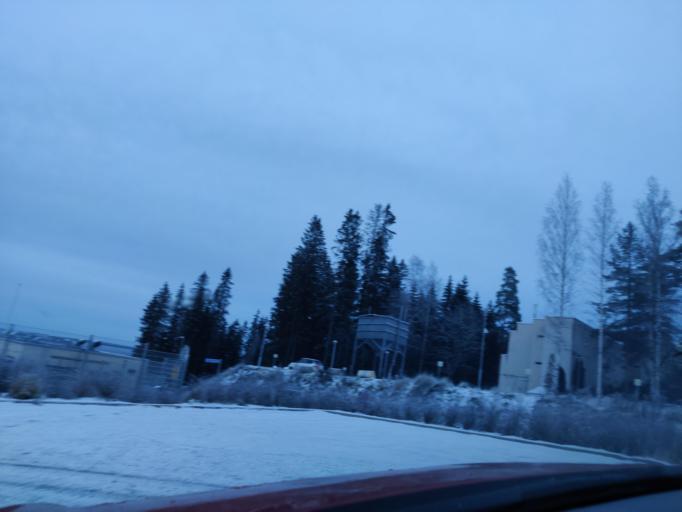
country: FI
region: Pirkanmaa
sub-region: Tampere
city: Tampere
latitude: 61.5130
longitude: 23.8037
